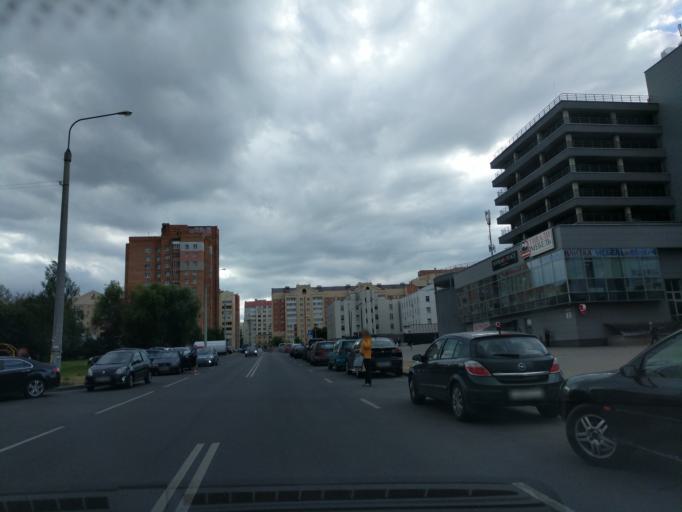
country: BY
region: Minsk
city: Novoye Medvezhino
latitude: 53.9067
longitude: 27.4849
